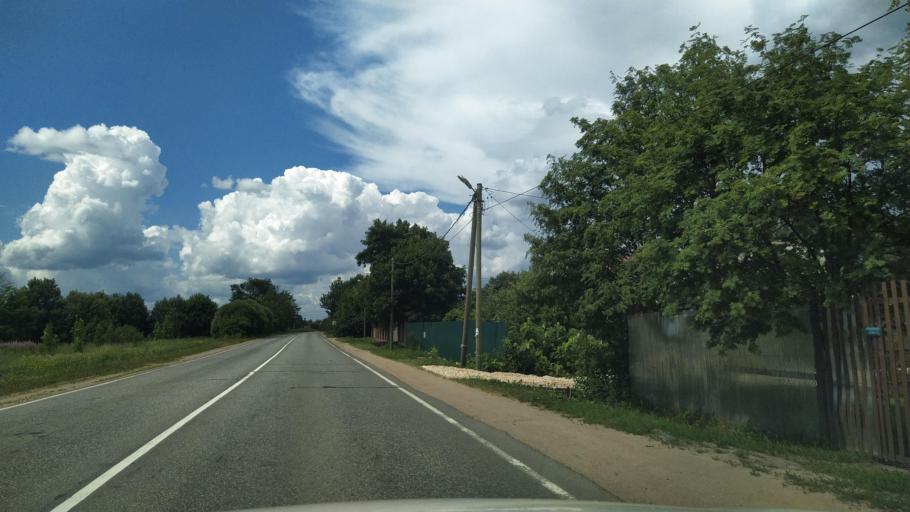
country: RU
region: Leningrad
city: Rozhdestveno
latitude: 59.3465
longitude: 29.9554
